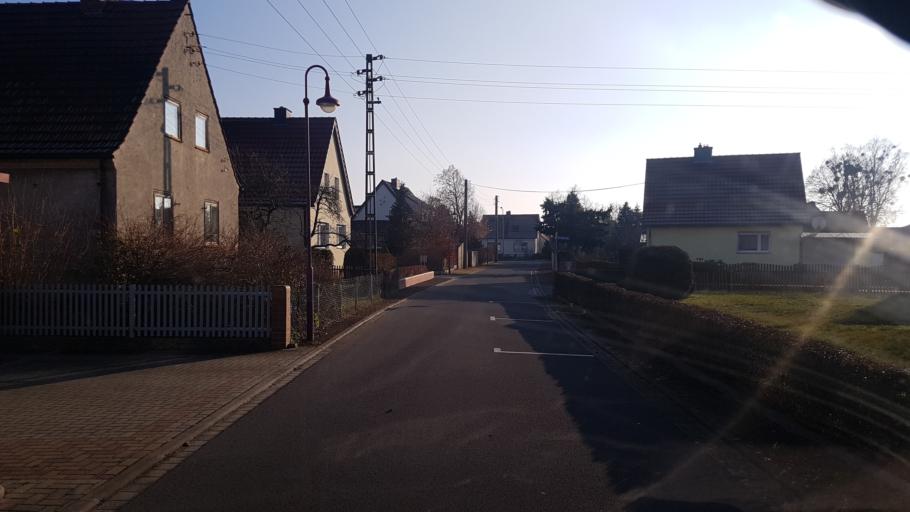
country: DE
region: Brandenburg
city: Lauchhammer
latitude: 51.4720
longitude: 13.7674
